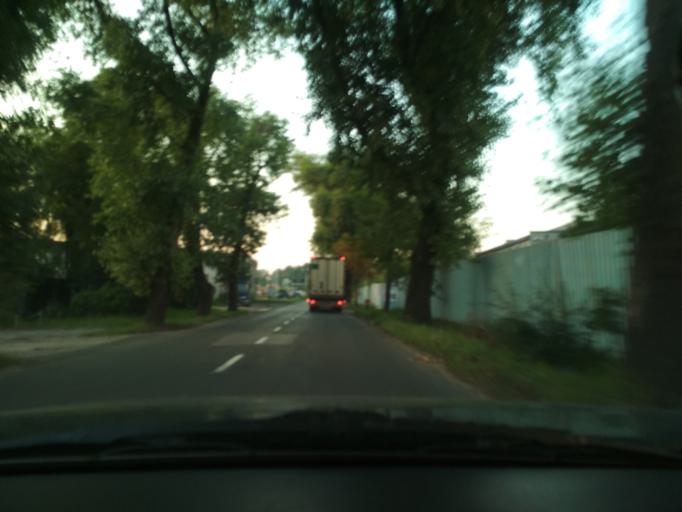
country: PL
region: Silesian Voivodeship
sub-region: Gliwice
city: Gliwice
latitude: 50.2684
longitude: 18.7027
